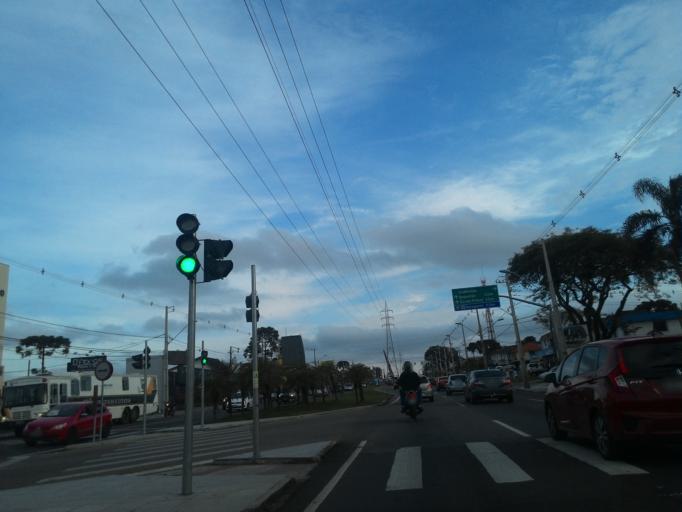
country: BR
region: Parana
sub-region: Curitiba
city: Curitiba
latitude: -25.4573
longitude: -49.2401
